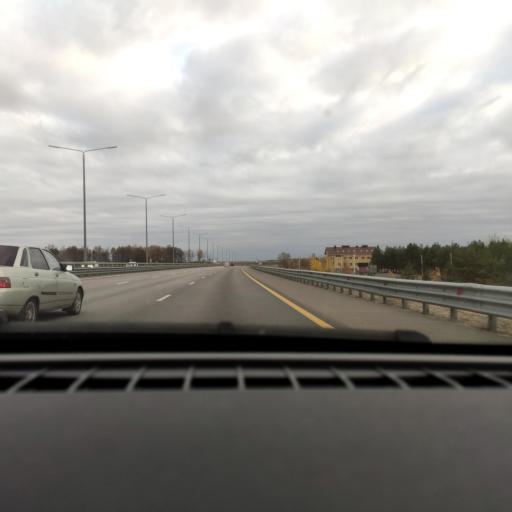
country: RU
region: Voronezj
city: Somovo
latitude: 51.7824
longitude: 39.2910
